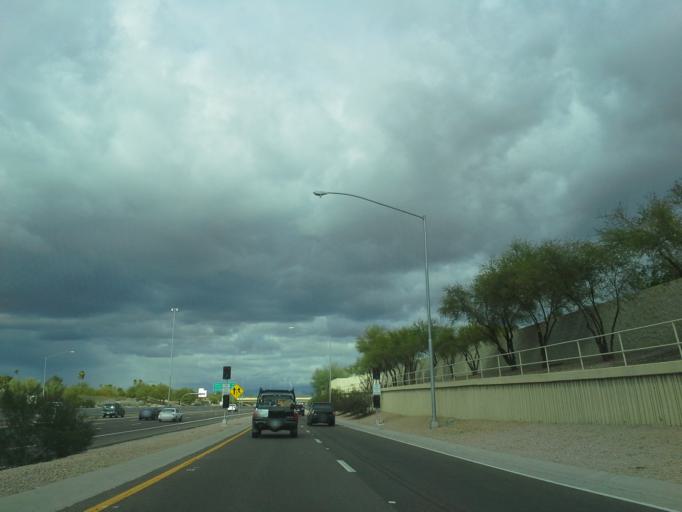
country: US
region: Arizona
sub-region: Maricopa County
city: Paradise Valley
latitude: 33.5848
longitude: -112.0094
